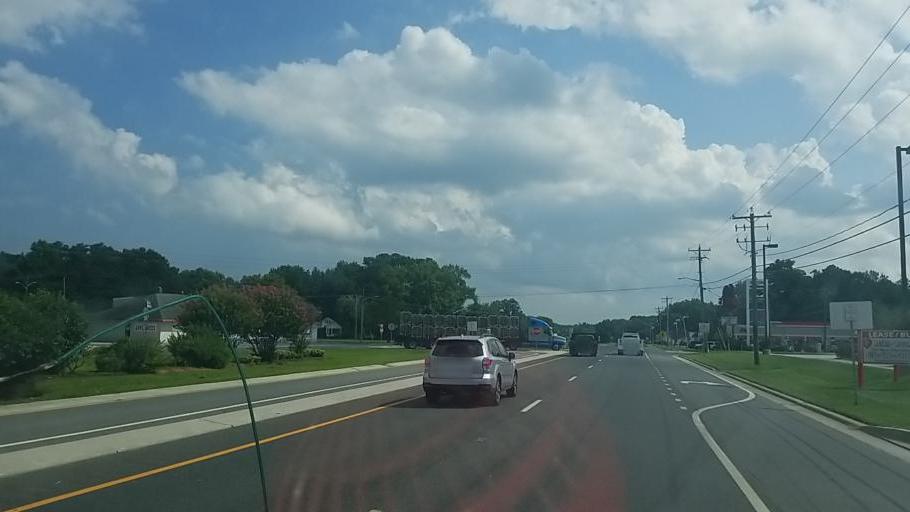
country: US
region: Delaware
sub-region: Sussex County
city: Selbyville
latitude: 38.4567
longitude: -75.2336
